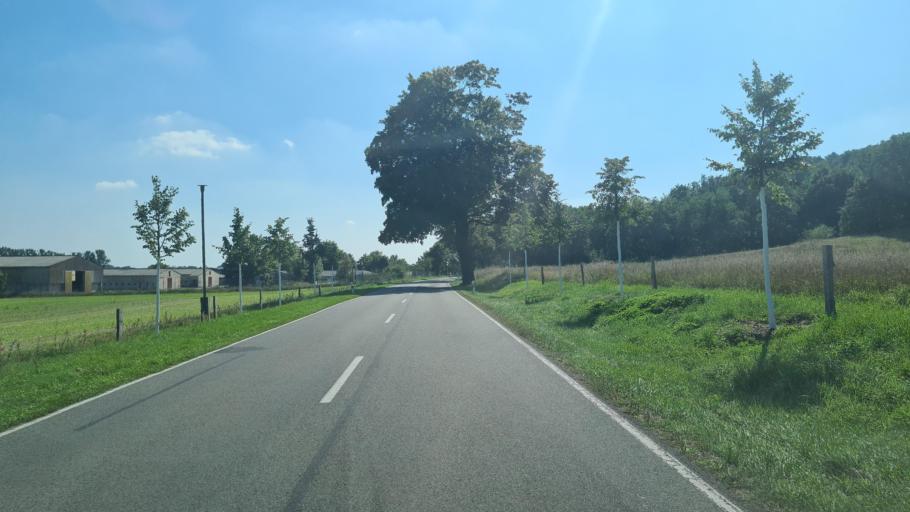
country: DE
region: Brandenburg
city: Pessin
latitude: 52.6984
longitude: 12.6485
